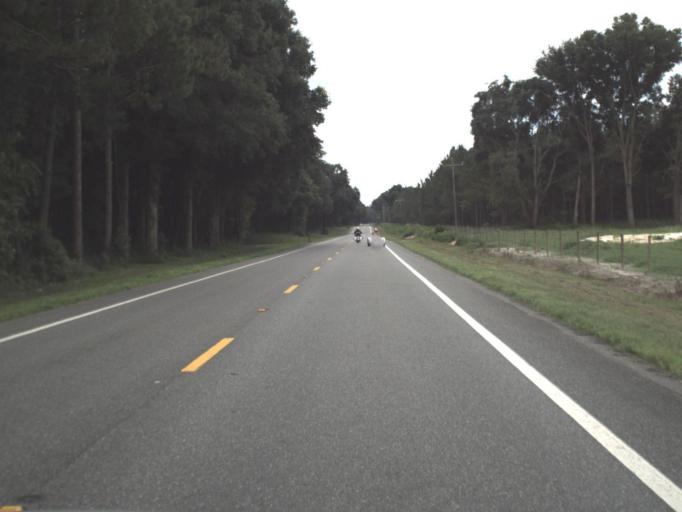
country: US
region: Florida
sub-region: Alachua County
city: Archer
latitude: 29.5568
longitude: -82.5322
